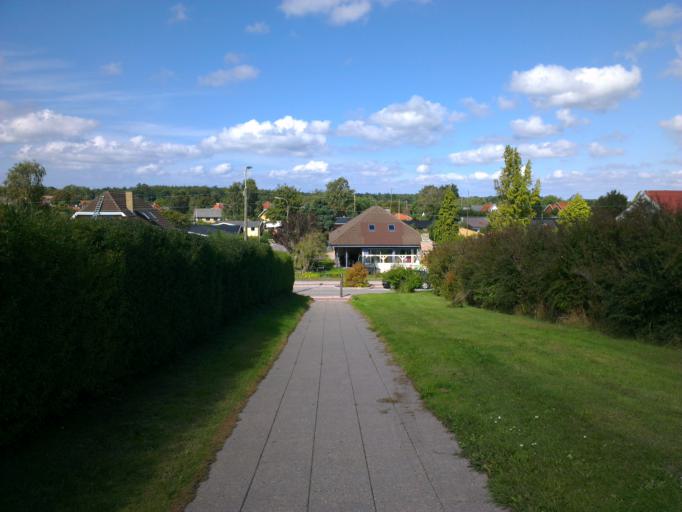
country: DK
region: Capital Region
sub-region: Frederikssund Kommune
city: Jaegerspris
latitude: 55.8518
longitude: 11.9921
